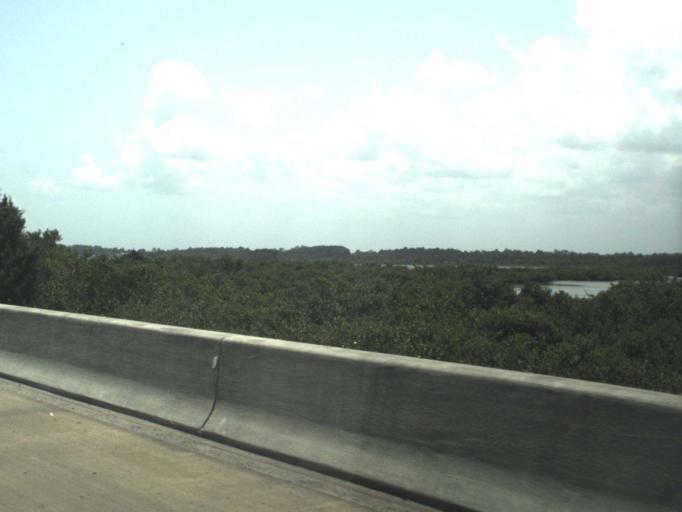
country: US
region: Florida
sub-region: Volusia County
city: Ponce Inlet
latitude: 29.0861
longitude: -80.9686
